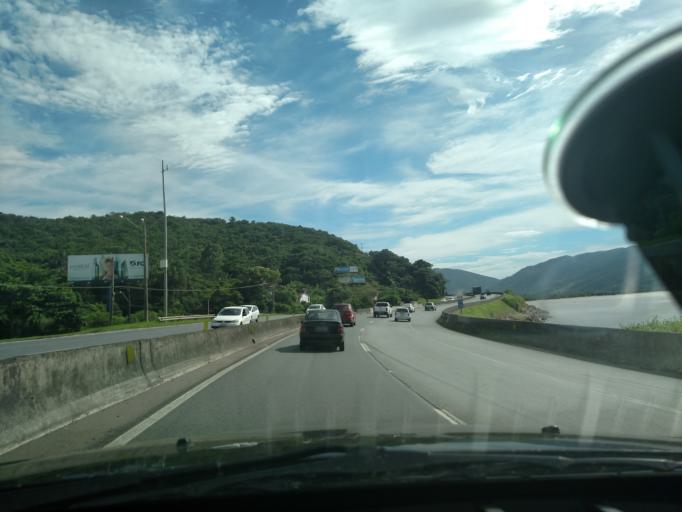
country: BR
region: Santa Catarina
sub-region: Biguacu
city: Biguacu
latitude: -27.4380
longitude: -48.6263
